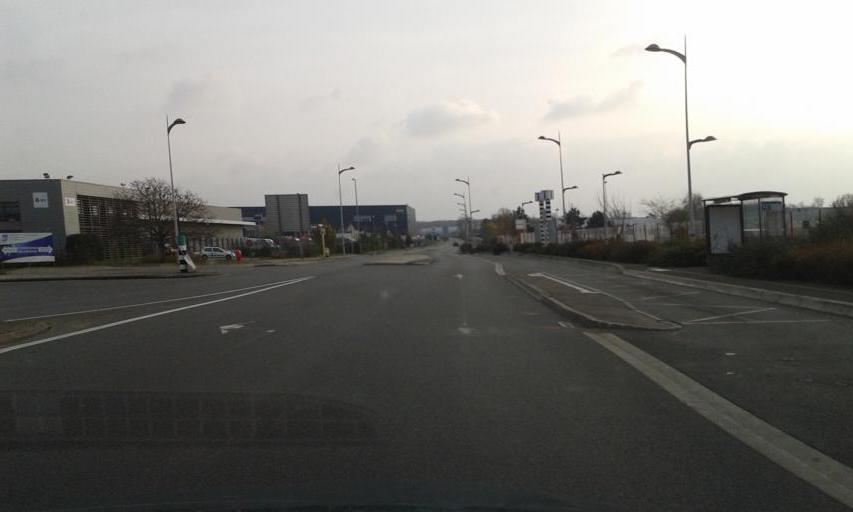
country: FR
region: Centre
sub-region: Departement du Loiret
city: Ormes
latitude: 47.9517
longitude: 1.8430
